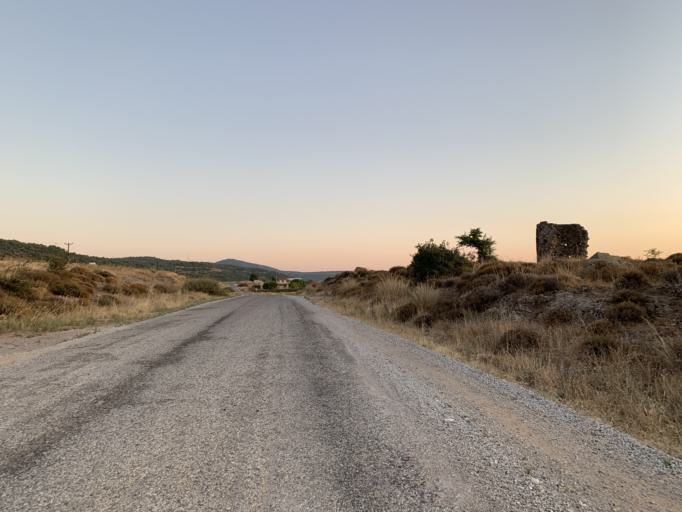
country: TR
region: Izmir
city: Uzunkuyu
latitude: 38.3279
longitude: 26.5838
